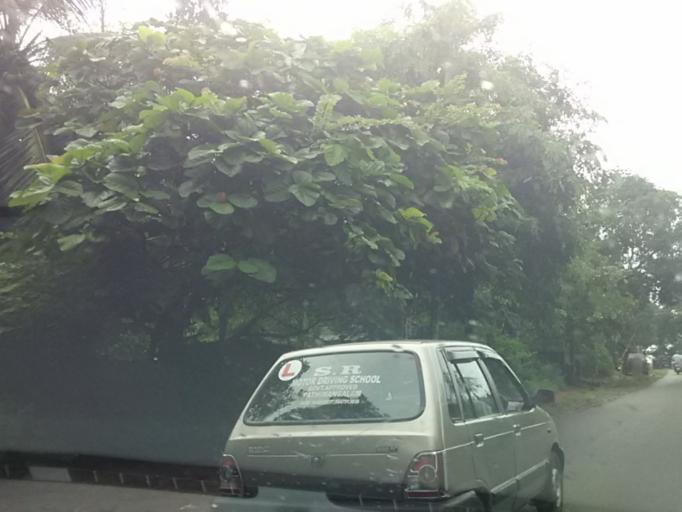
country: IN
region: Kerala
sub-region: Kozhikode
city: Kunnamangalam
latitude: 11.3087
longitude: 75.9055
